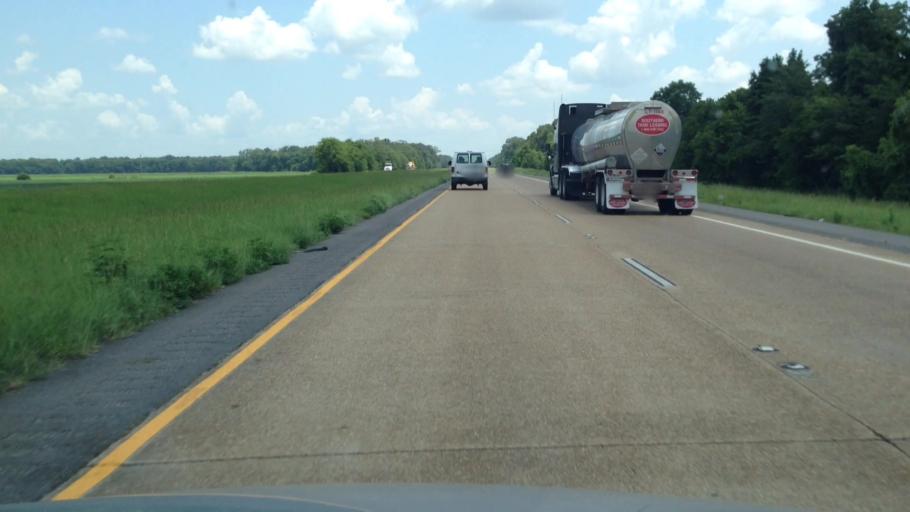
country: US
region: Louisiana
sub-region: Rapides Parish
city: Lecompte
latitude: 31.0037
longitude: -92.3487
